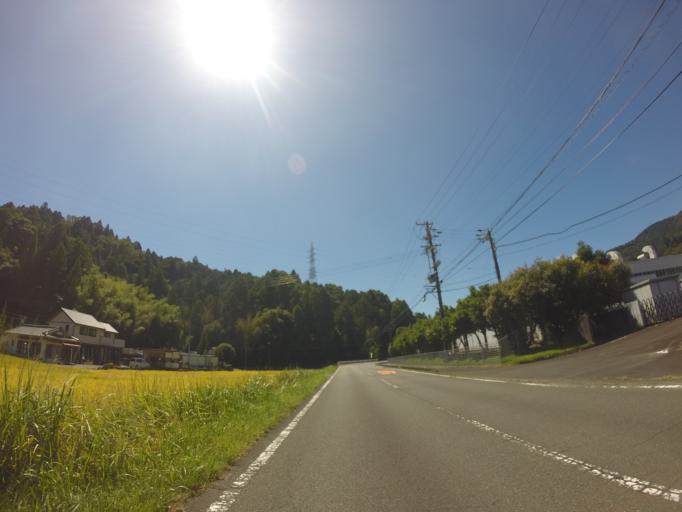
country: JP
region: Shizuoka
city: Kanaya
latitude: 34.8762
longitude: 138.1393
